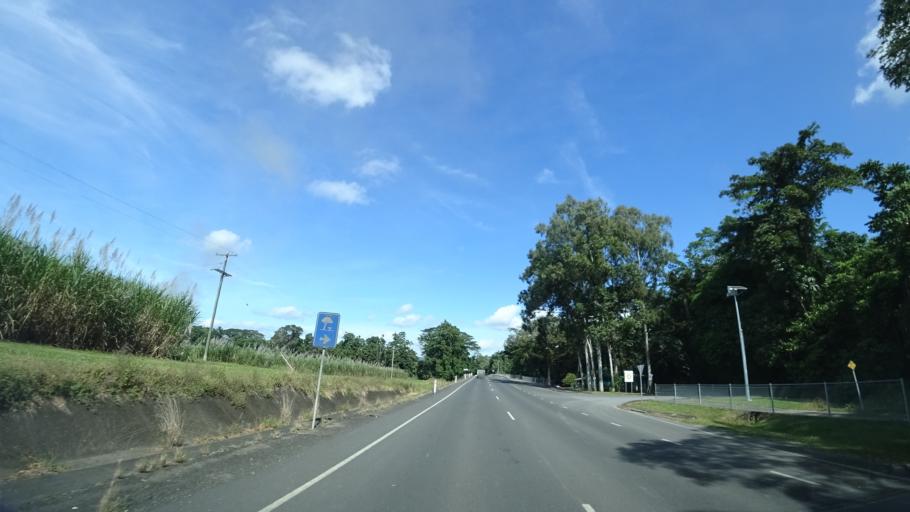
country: AU
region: Queensland
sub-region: Cairns
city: Port Douglas
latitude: -16.4511
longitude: 145.3719
